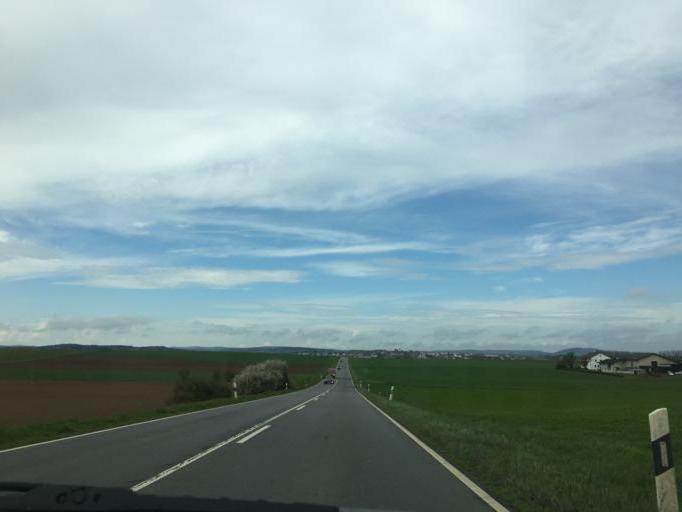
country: DE
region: Hesse
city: Reinheim
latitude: 49.8328
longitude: 8.8683
